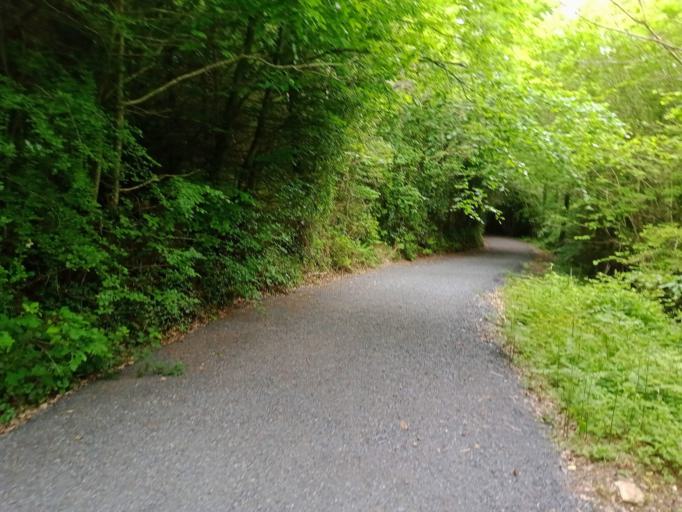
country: IE
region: Leinster
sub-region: Kilkenny
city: Thomastown
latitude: 52.4700
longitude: -7.0459
